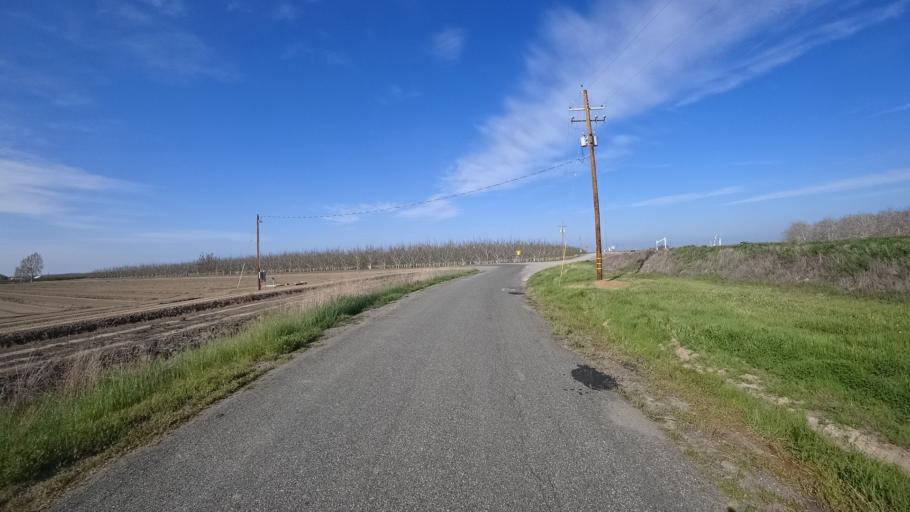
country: US
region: California
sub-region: Glenn County
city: Hamilton City
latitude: 39.6302
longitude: -122.0451
